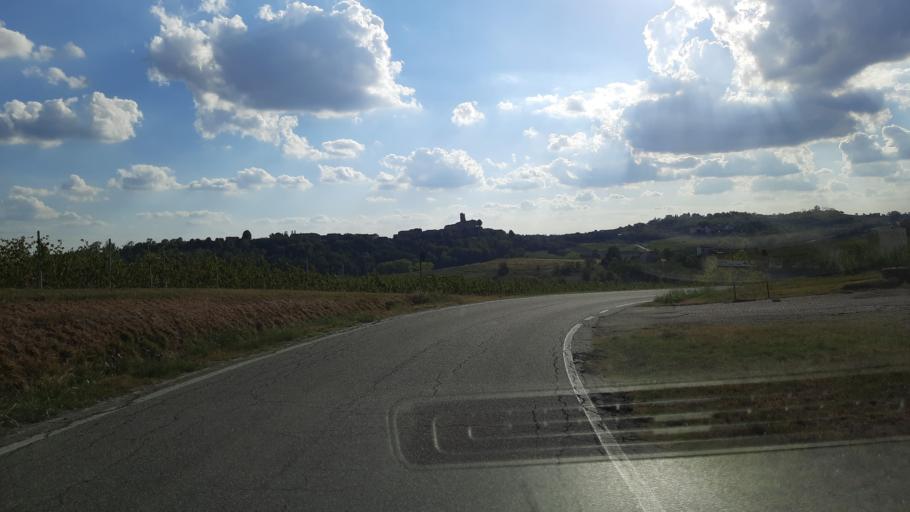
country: IT
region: Piedmont
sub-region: Provincia di Alessandria
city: Ottiglio
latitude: 45.0459
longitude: 8.3268
